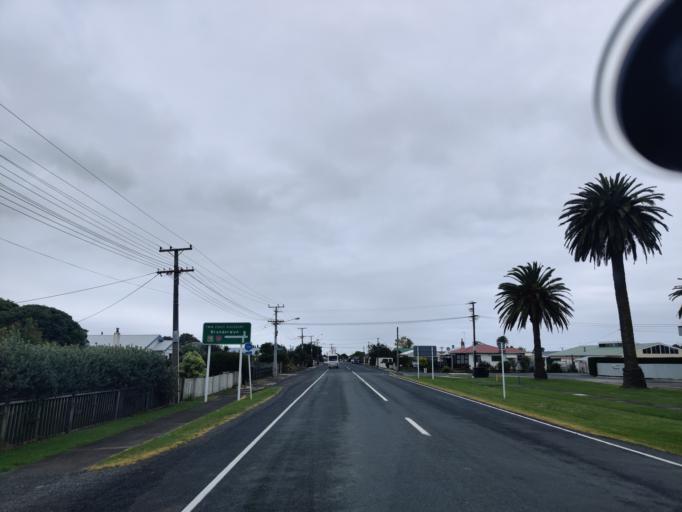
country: NZ
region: Northland
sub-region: Kaipara District
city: Dargaville
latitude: -36.1343
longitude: 174.0221
